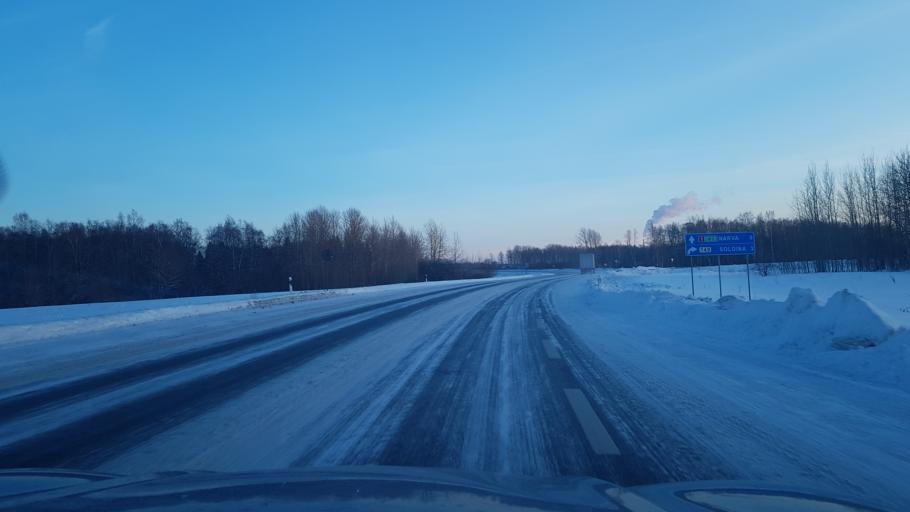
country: EE
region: Ida-Virumaa
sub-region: Narva-Joesuu linn
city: Narva-Joesuu
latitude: 59.3969
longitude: 28.0775
